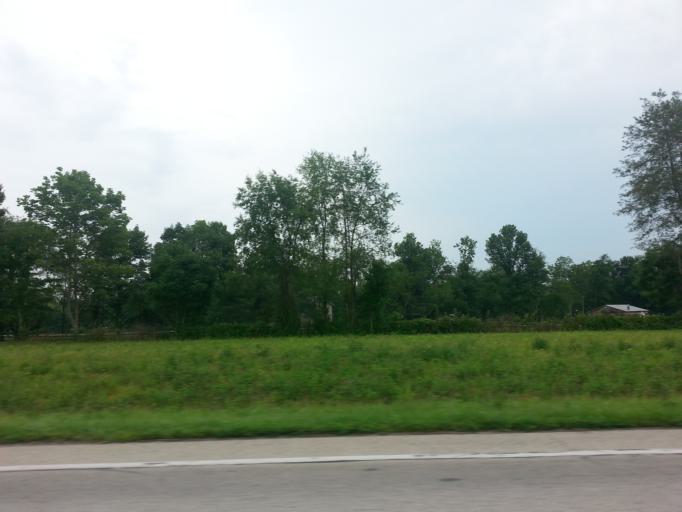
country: US
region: Ohio
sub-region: Brown County
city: Ripley
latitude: 38.8151
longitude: -83.8086
